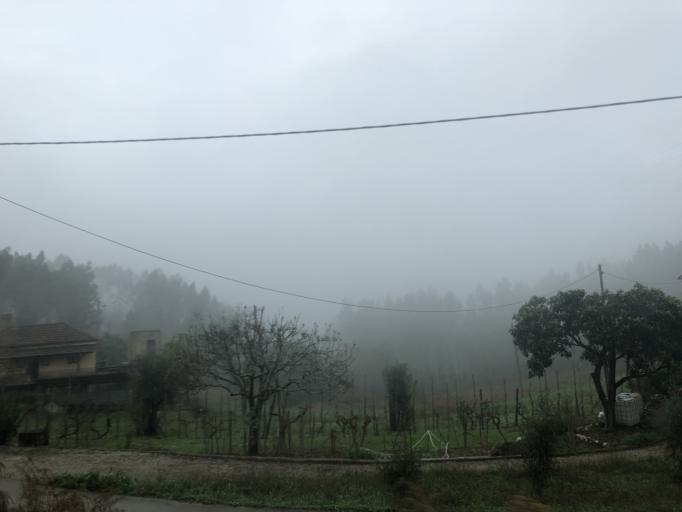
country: PT
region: Viseu
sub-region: Mortagua
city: Mortagua
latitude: 40.3902
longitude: -8.2884
